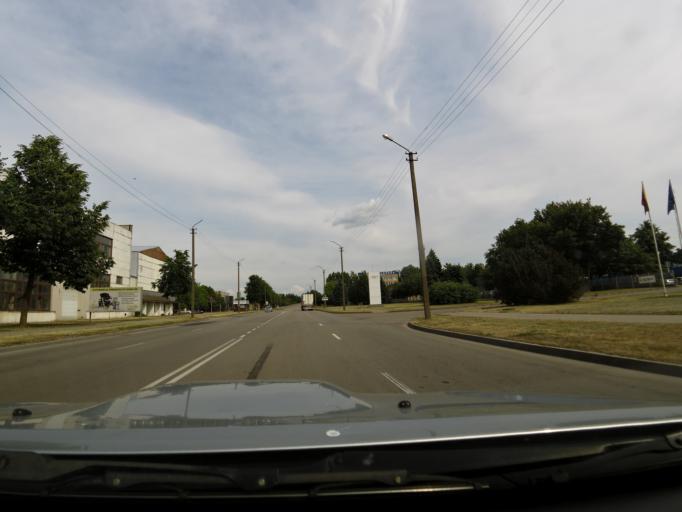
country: LT
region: Marijampoles apskritis
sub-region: Marijampole Municipality
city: Marijampole
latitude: 54.5748
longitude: 23.3748
